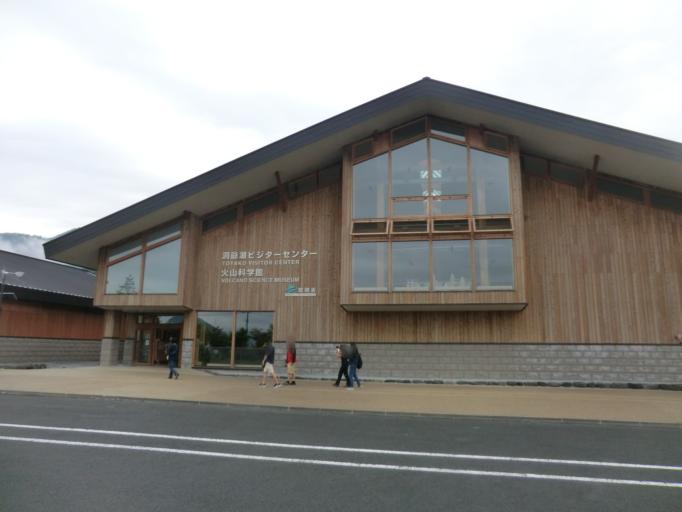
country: JP
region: Hokkaido
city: Date
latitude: 42.5643
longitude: 140.8150
